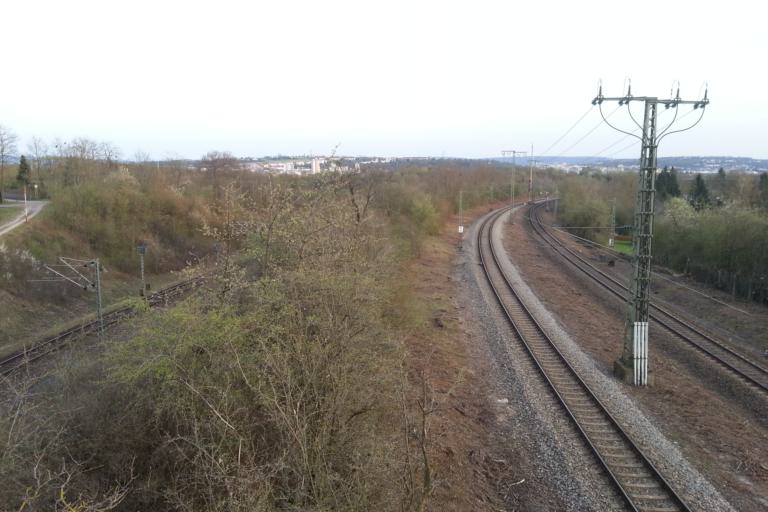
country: DE
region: Baden-Wuerttemberg
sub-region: Regierungsbezirk Stuttgart
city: Kornwestheim
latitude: 48.8467
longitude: 9.1735
